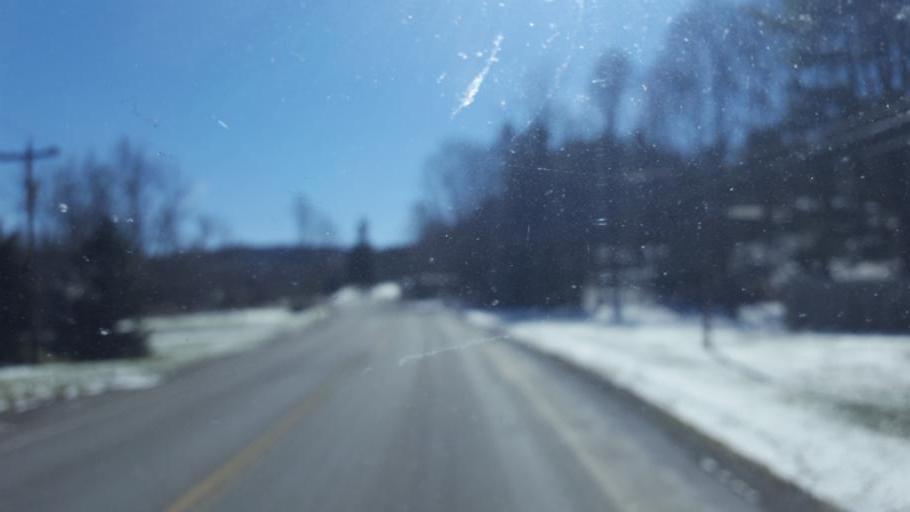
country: US
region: New York
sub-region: Allegany County
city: Wellsville
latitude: 42.0810
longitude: -77.9079
